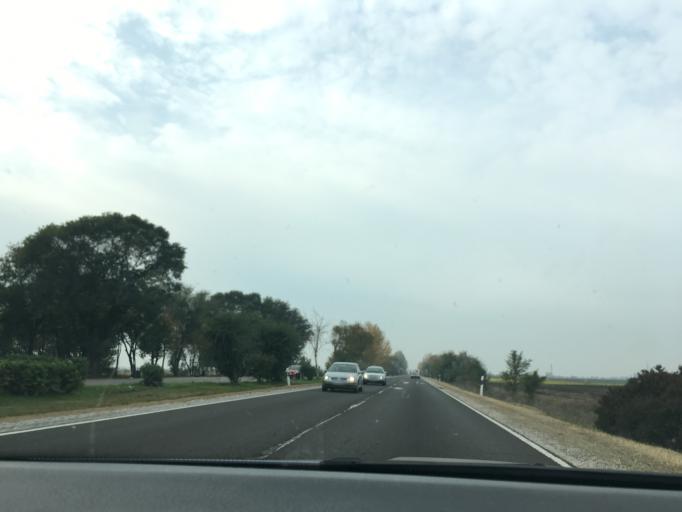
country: HU
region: Jasz-Nagykun-Szolnok
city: Toszeg
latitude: 47.1554
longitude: 20.1224
